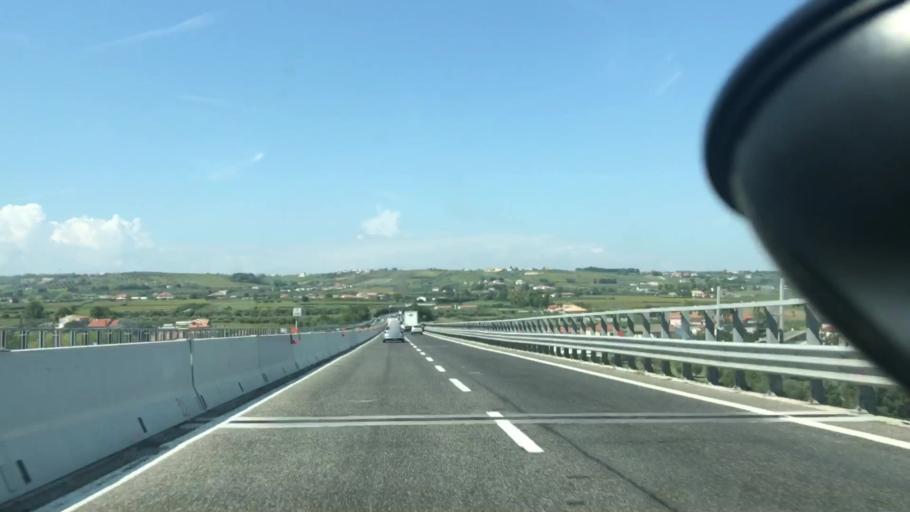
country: IT
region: Abruzzo
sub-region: Provincia di Chieti
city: Miglianico
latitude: 42.3748
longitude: 14.3050
